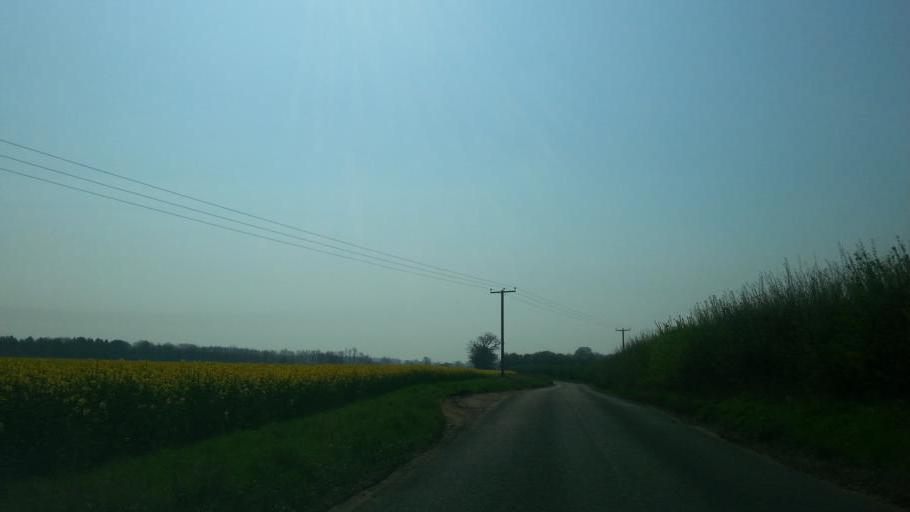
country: GB
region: England
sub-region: Suffolk
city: Thurston
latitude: 52.2405
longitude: 0.8071
